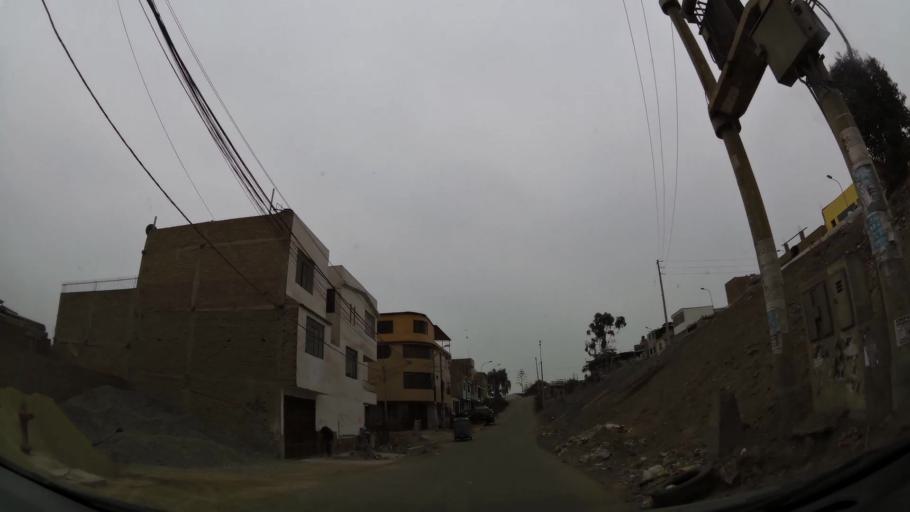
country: PE
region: Lima
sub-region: Lima
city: Surco
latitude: -12.1790
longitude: -76.9820
